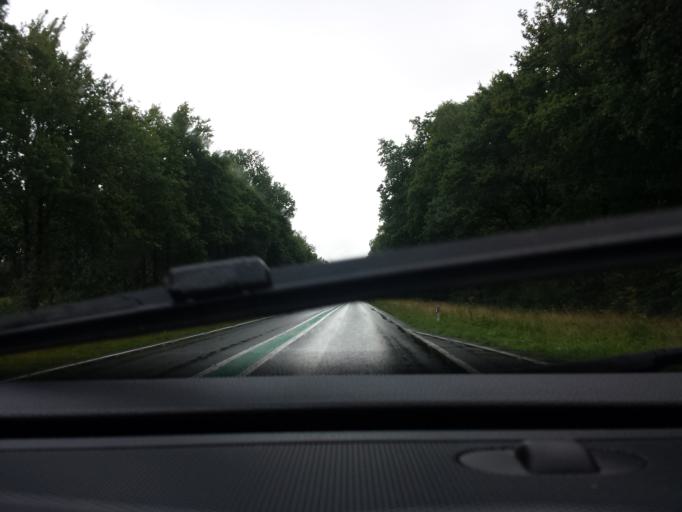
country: NL
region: Gelderland
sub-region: Gemeente Lochem
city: Laren
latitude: 52.2074
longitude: 6.3773
